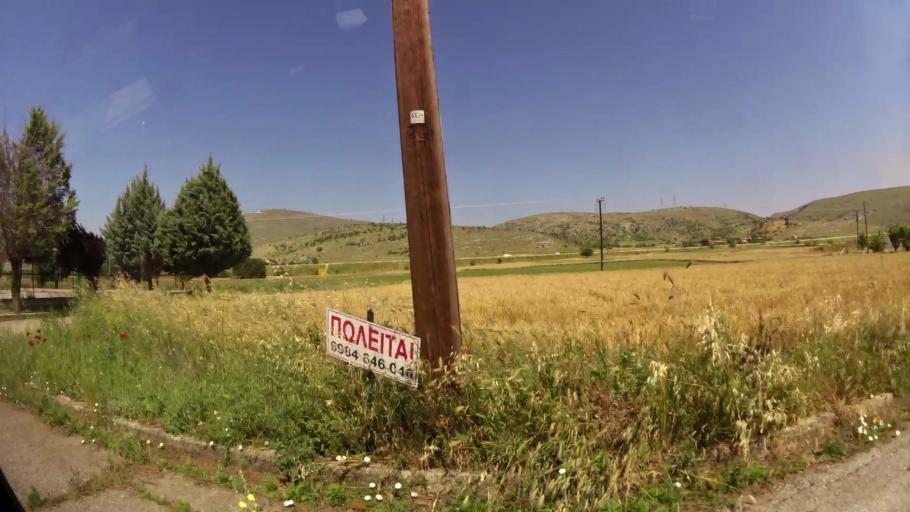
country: GR
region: West Macedonia
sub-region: Nomos Kozanis
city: Koila
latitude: 40.3379
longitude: 21.7857
